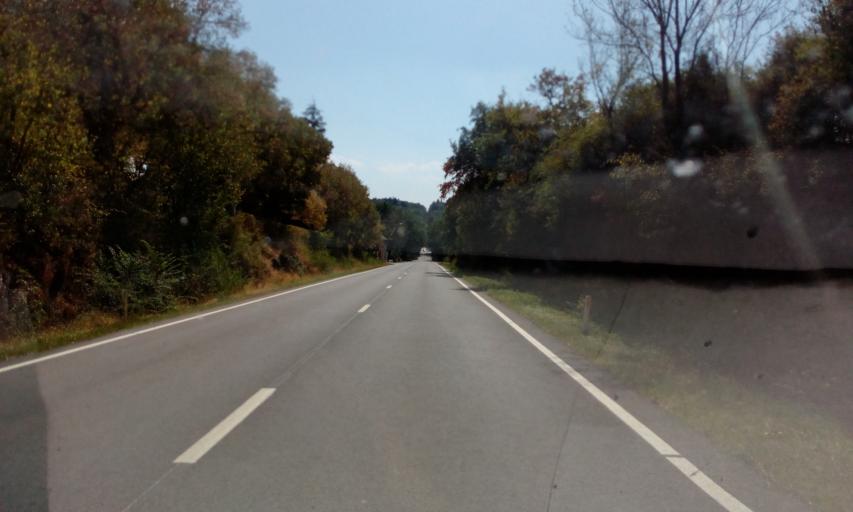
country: BE
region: Wallonia
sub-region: Province de Namur
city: Houyet
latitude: 50.1633
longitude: 5.0777
